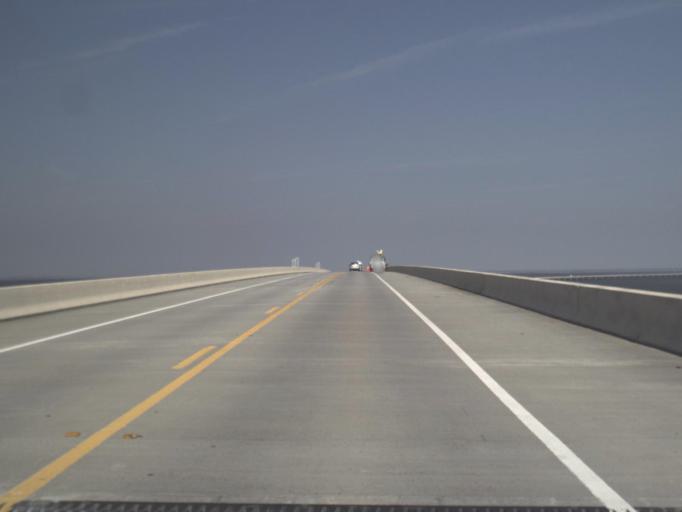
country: US
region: Florida
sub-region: Franklin County
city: Eastpoint
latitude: 29.6825
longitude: -84.8791
